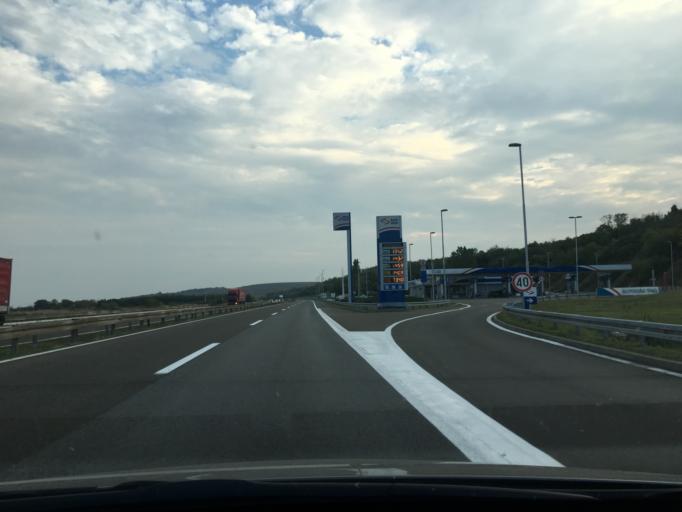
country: RS
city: Lugavcina
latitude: 44.4707
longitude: 21.0386
